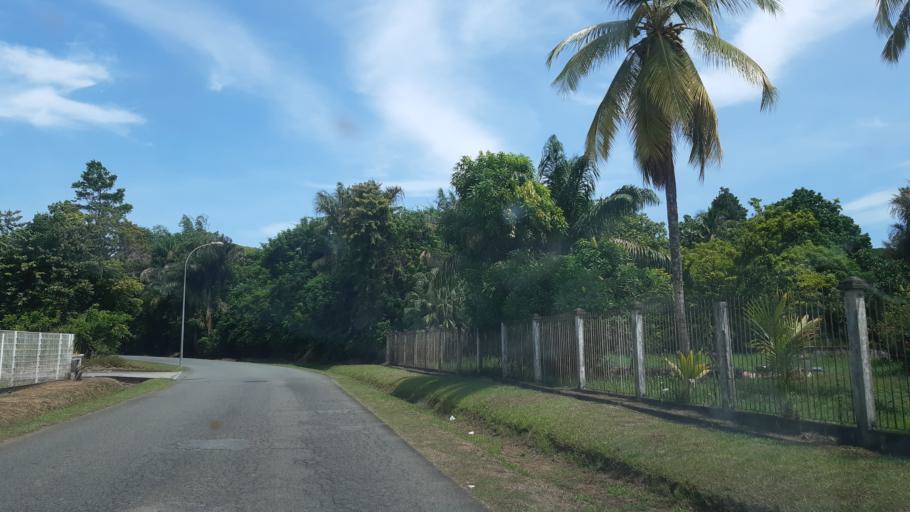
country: GF
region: Guyane
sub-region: Guyane
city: Cayenne
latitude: 4.9295
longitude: -52.2991
